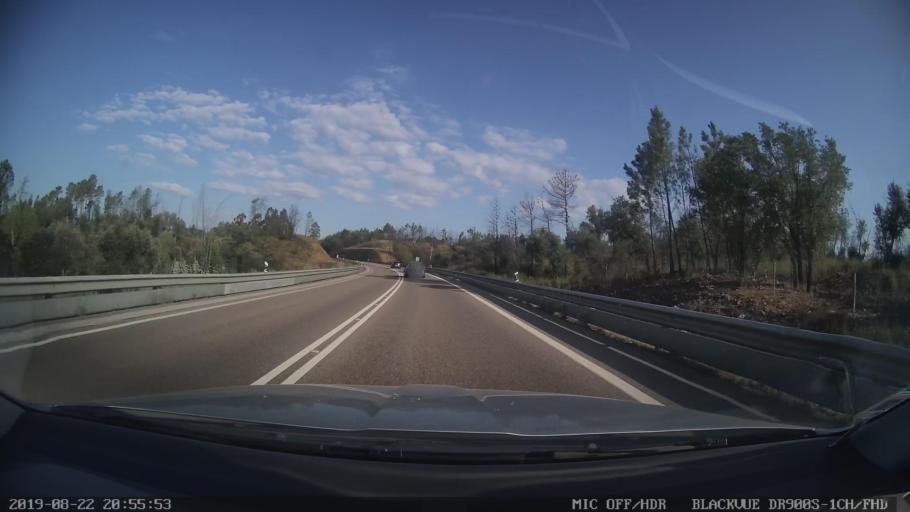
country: PT
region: Castelo Branco
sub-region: Serta
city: Serta
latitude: 39.7849
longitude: -8.0411
